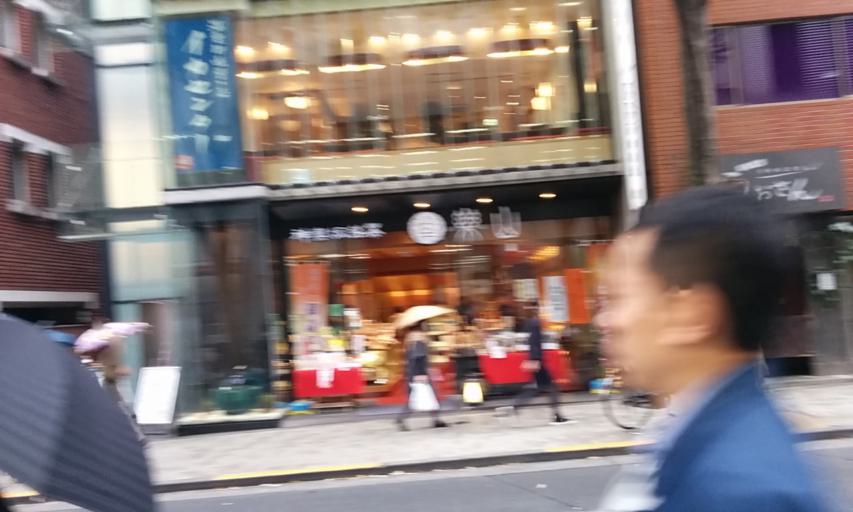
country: JP
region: Tokyo
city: Tokyo
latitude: 35.7017
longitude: 139.7396
